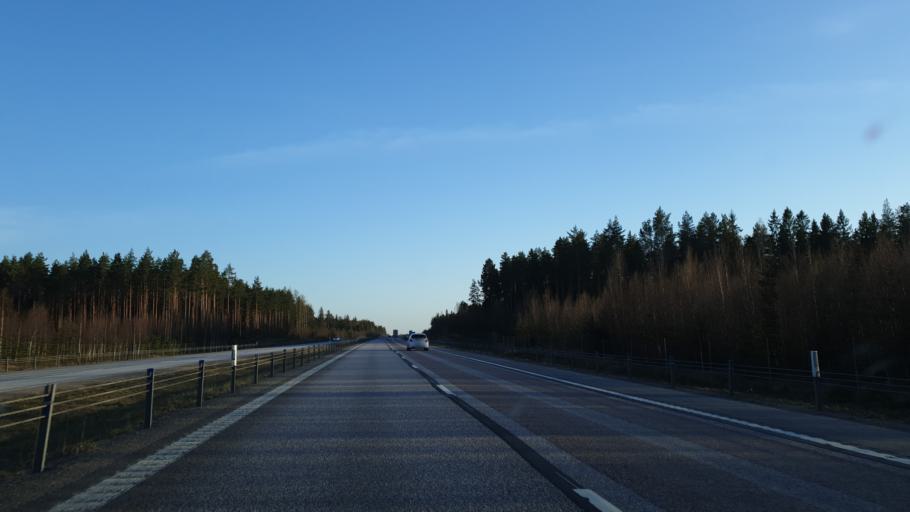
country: SE
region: Uppsala
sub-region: Tierps Kommun
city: Tierp
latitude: 60.2307
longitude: 17.5006
